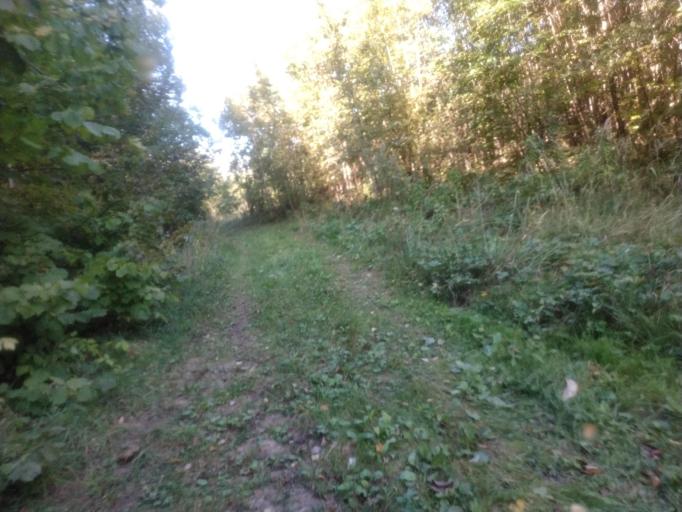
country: RU
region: Chuvashia
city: Novyye Lapsary
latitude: 56.1412
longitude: 47.1374
